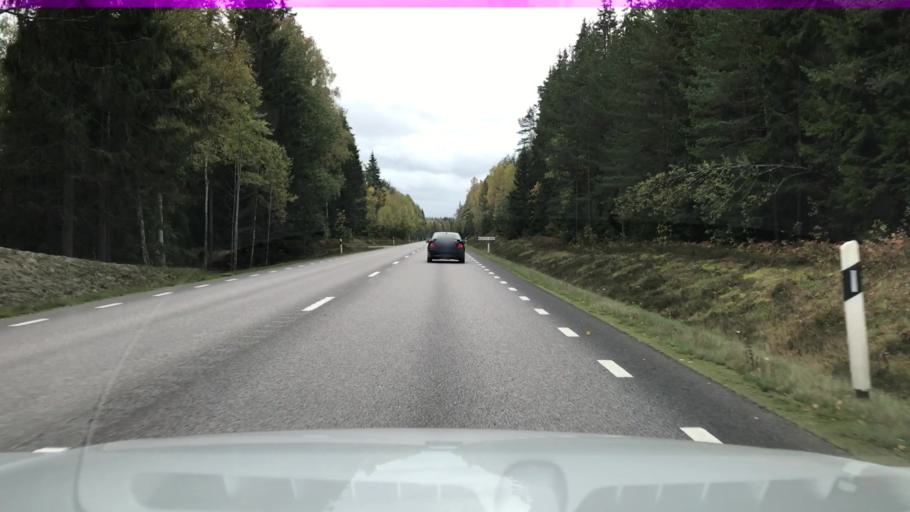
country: SE
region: Kalmar
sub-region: Hultsfreds Kommun
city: Hultsfred
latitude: 57.5481
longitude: 15.8455
